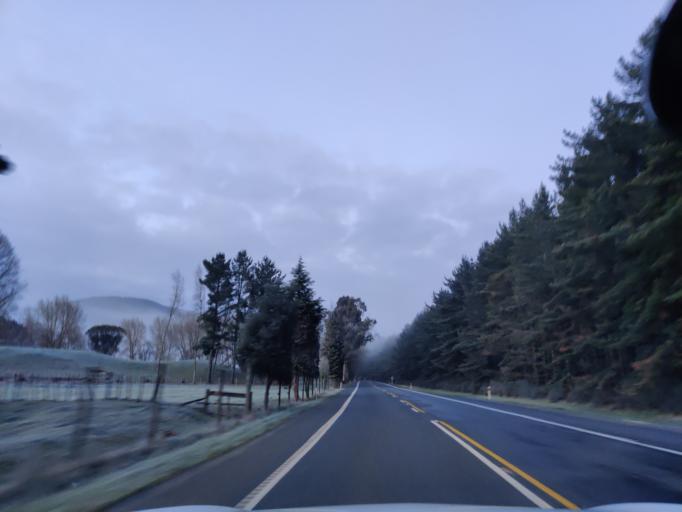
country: NZ
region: Waikato
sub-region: South Waikato District
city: Tokoroa
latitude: -38.3492
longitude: 176.0055
